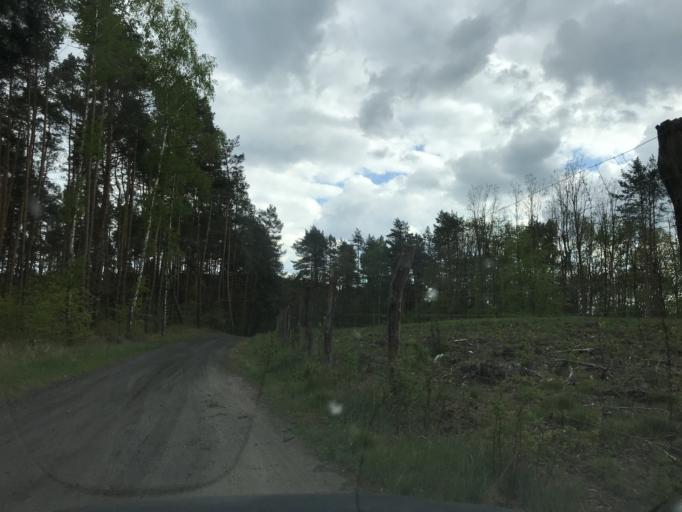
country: PL
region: West Pomeranian Voivodeship
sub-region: Powiat mysliborski
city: Mysliborz
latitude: 52.8626
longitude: 14.8868
